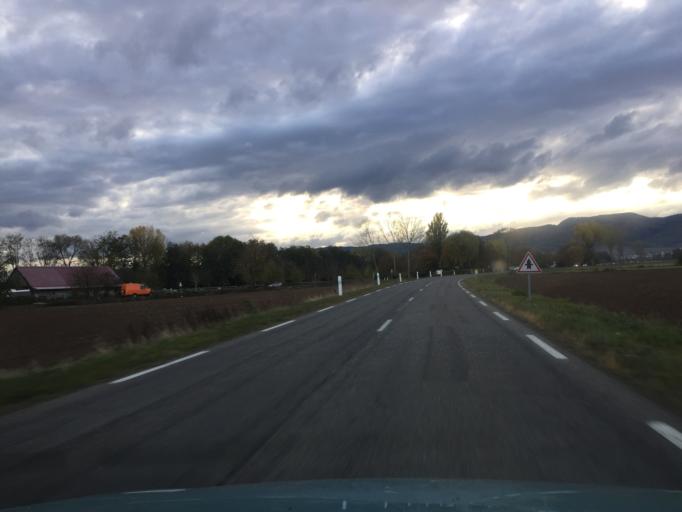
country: FR
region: Alsace
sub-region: Departement du Haut-Rhin
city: Bergheim
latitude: 48.1891
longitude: 7.3661
